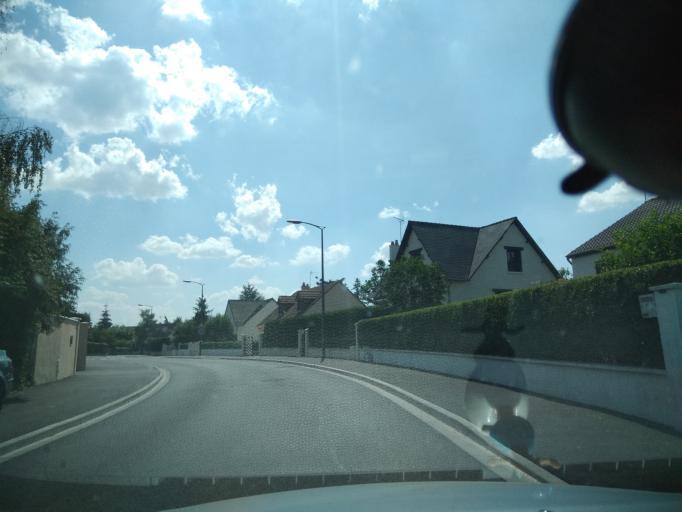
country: FR
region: Centre
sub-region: Departement d'Indre-et-Loire
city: Chambray-les-Tours
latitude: 47.3480
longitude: 0.6904
